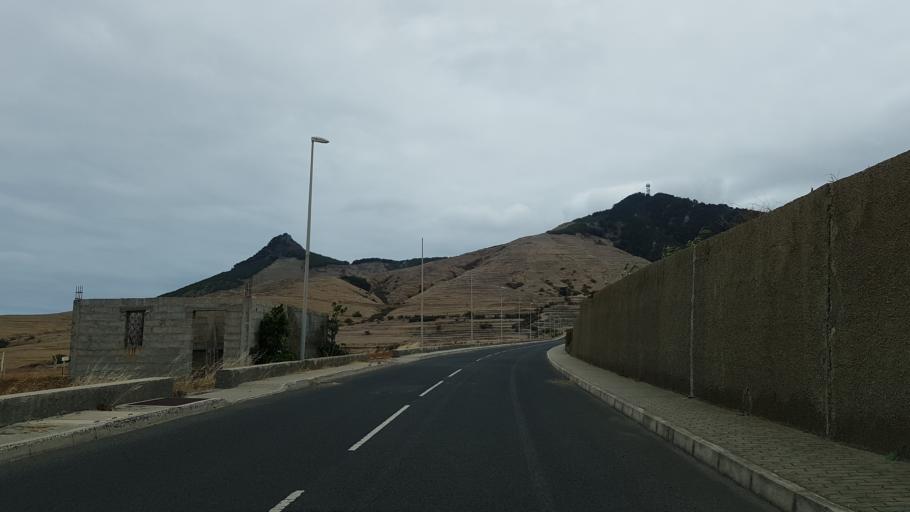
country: PT
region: Madeira
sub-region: Porto Santo
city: Camacha
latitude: 33.0897
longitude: -16.3411
